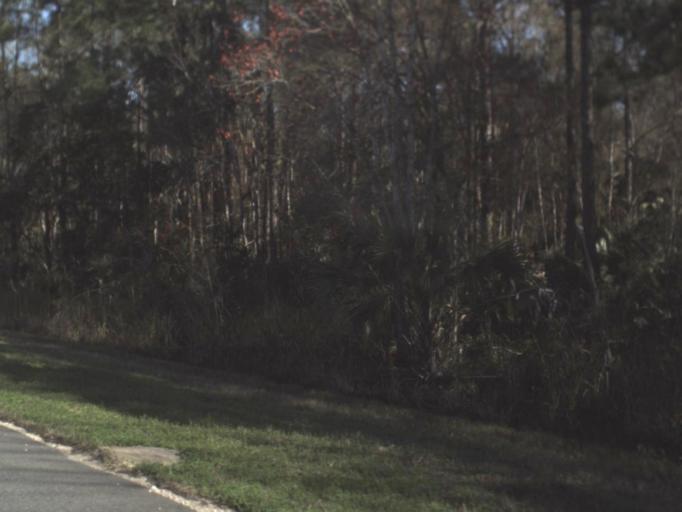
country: US
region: Florida
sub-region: Leon County
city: Woodville
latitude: 30.1695
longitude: -84.0068
